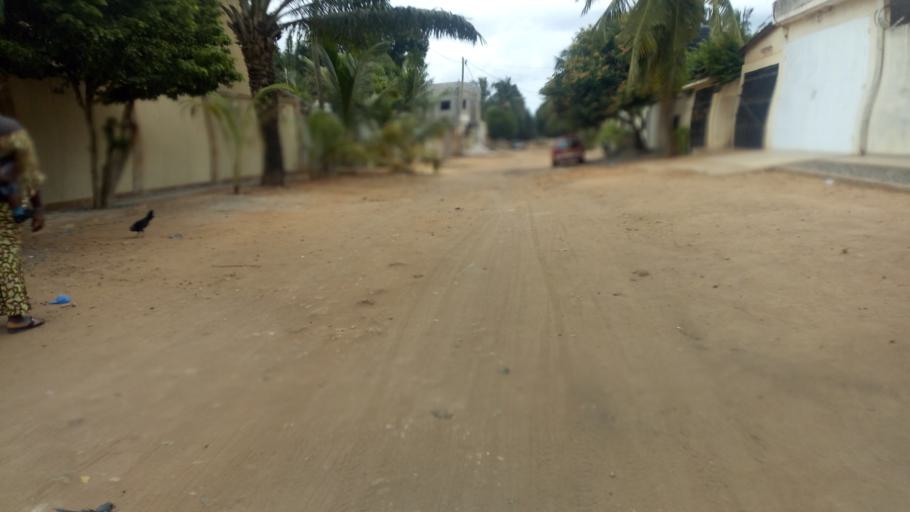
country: TG
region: Maritime
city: Lome
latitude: 6.2334
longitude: 1.1833
